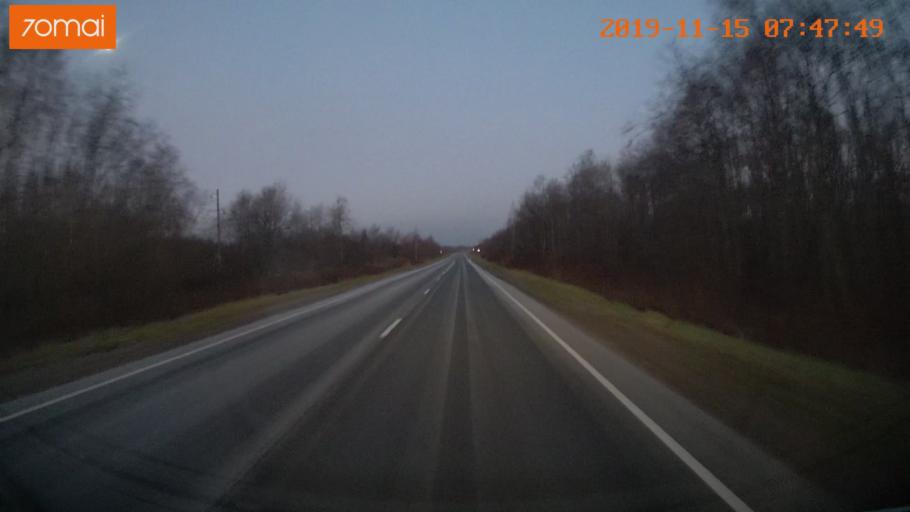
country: RU
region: Vologda
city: Sheksna
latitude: 58.8451
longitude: 38.2541
